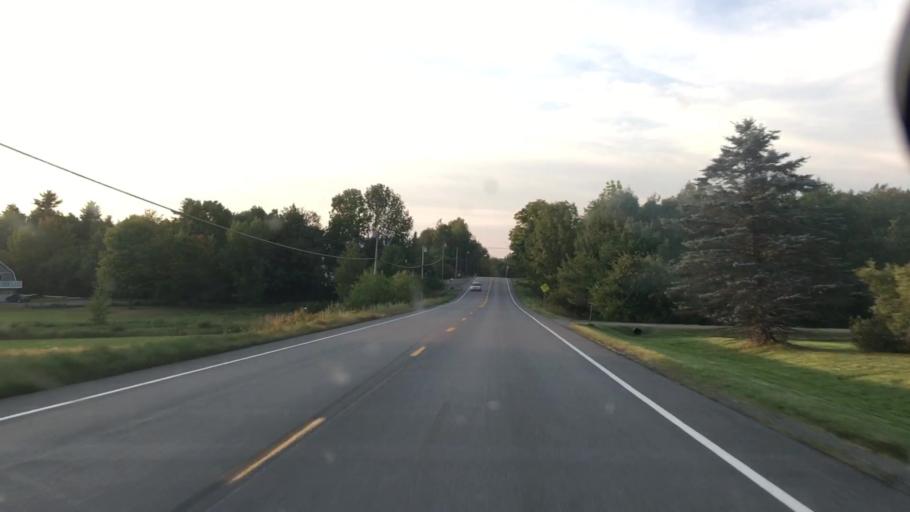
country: US
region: Maine
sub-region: Penobscot County
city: Hermon
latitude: 44.7371
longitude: -68.9649
